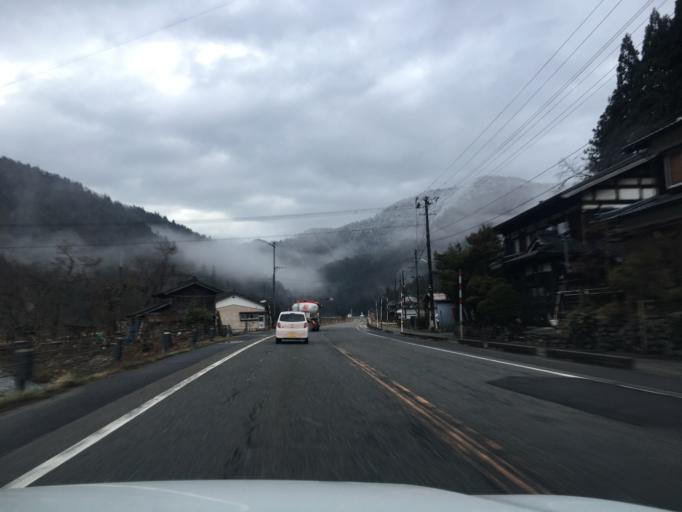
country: JP
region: Niigata
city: Murakami
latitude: 38.4570
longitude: 139.5749
